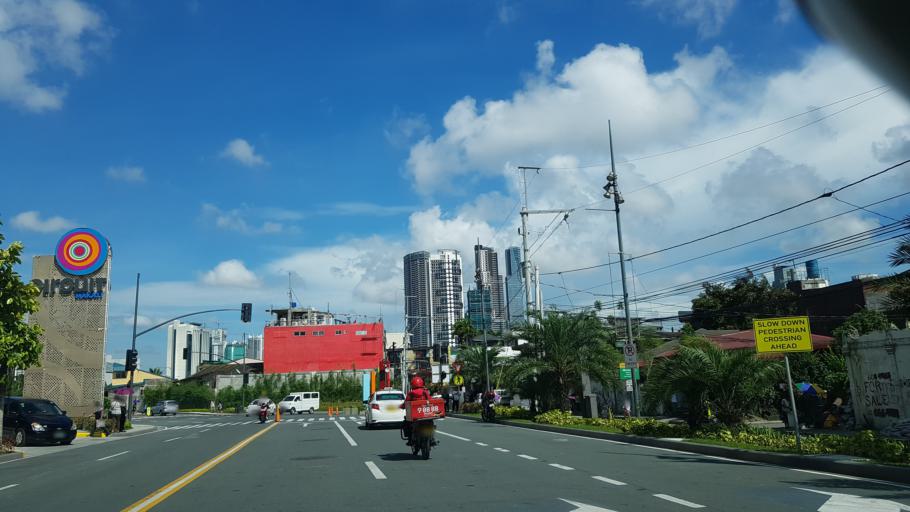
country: PH
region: Metro Manila
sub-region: Mandaluyong
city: Mandaluyong City
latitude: 14.5722
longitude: 121.0184
